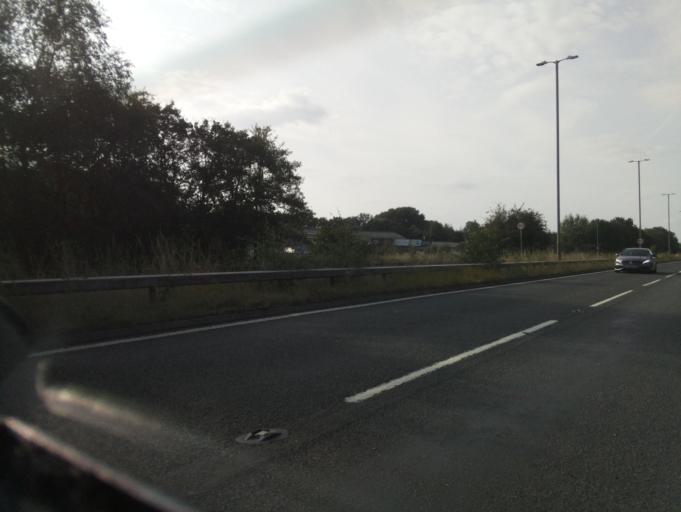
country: GB
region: England
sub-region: Solihull
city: Tidbury Green
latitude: 52.3484
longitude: -1.8796
